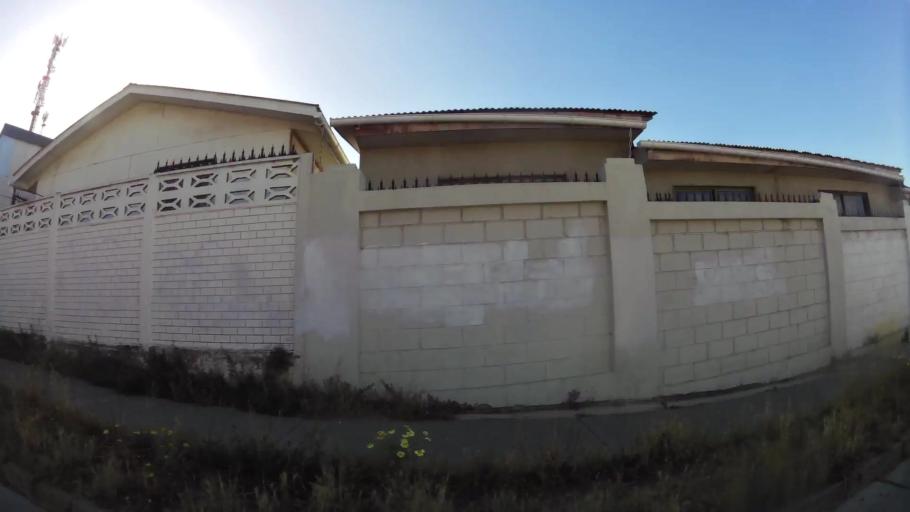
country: CL
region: Valparaiso
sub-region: Provincia de Valparaiso
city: Vina del Mar
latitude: -33.0323
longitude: -71.5691
